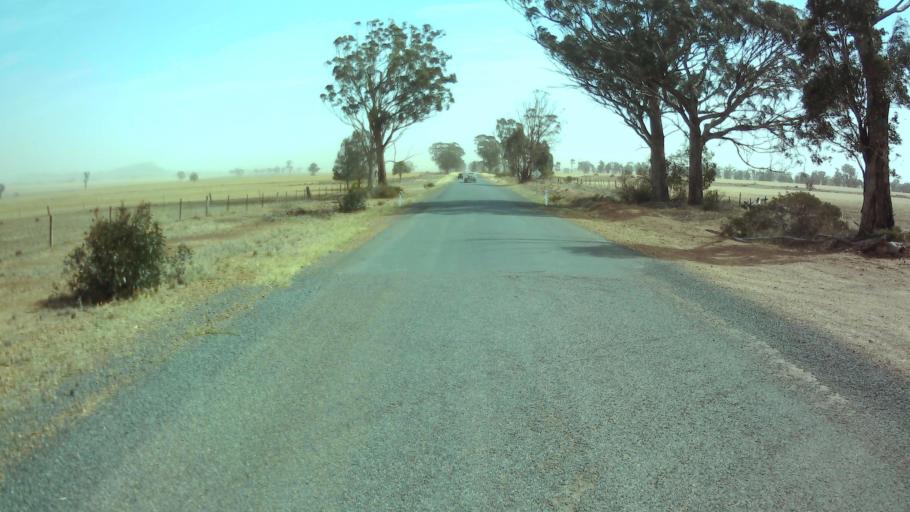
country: AU
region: New South Wales
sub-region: Weddin
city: Grenfell
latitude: -33.7730
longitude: 147.9864
